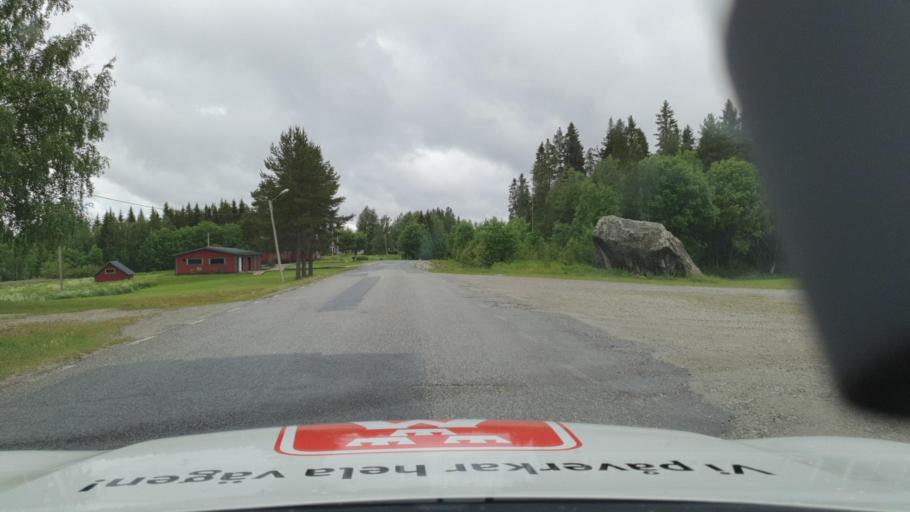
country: SE
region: Vaesterbotten
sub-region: Dorotea Kommun
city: Dorotea
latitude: 64.1145
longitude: 16.6356
